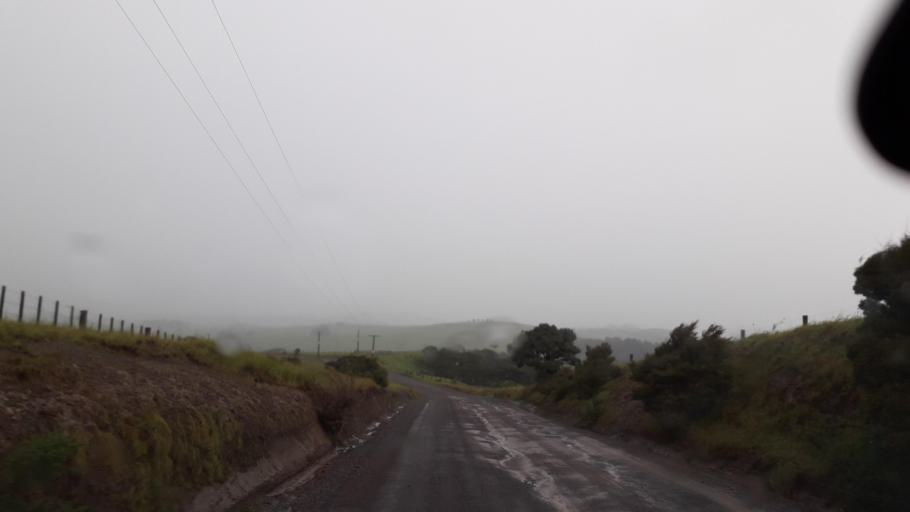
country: NZ
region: Northland
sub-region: Far North District
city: Kerikeri
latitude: -35.1338
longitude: 174.0165
